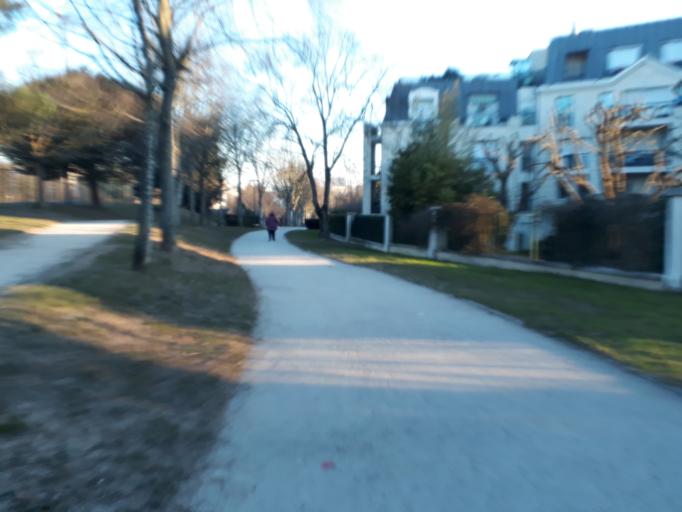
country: FR
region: Ile-de-France
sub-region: Departement des Hauts-de-Seine
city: Fontenay-aux-Roses
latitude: 48.7918
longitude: 2.2927
